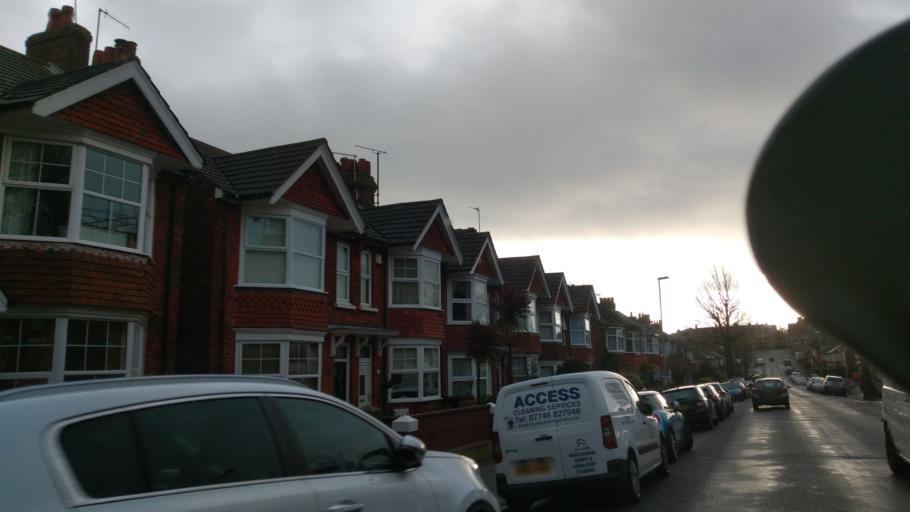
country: GB
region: England
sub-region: East Sussex
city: Eastbourne
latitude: 50.7747
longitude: 0.2602
